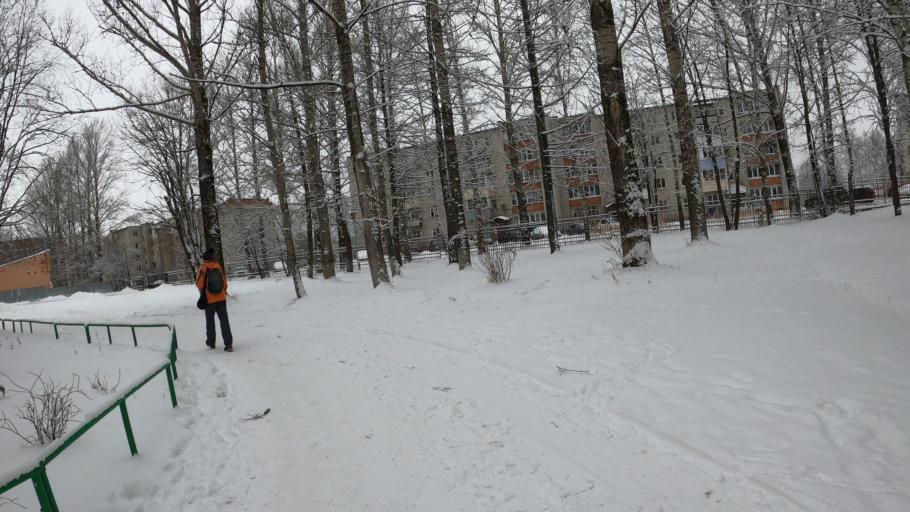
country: RU
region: Jaroslavl
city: Pereslavl'-Zalesskiy
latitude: 56.7553
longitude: 38.8711
